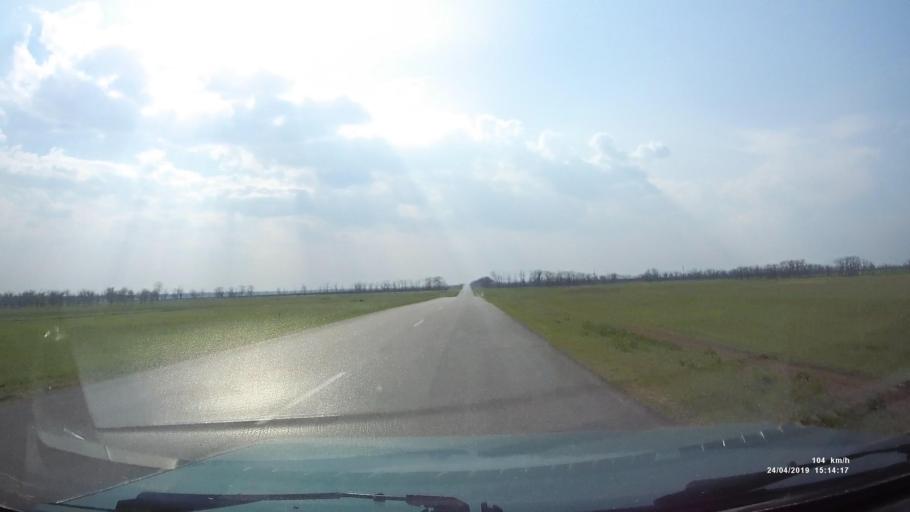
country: RU
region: Rostov
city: Remontnoye
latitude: 46.5466
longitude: 43.2621
